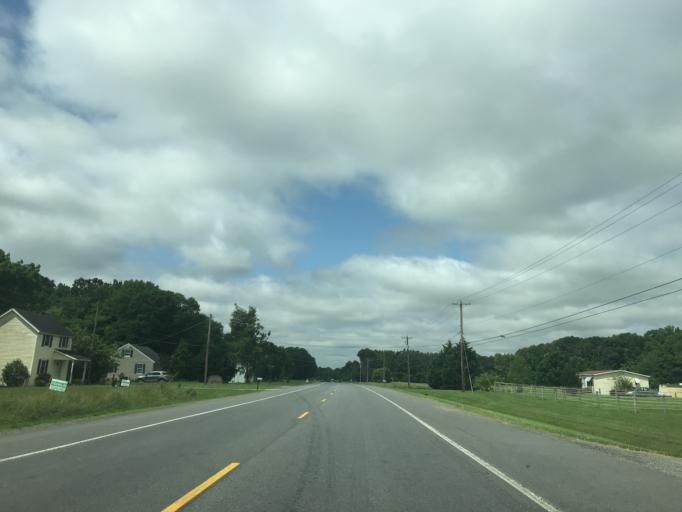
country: US
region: Maryland
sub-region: Caroline County
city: Ridgely
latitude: 38.9264
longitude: -75.9254
